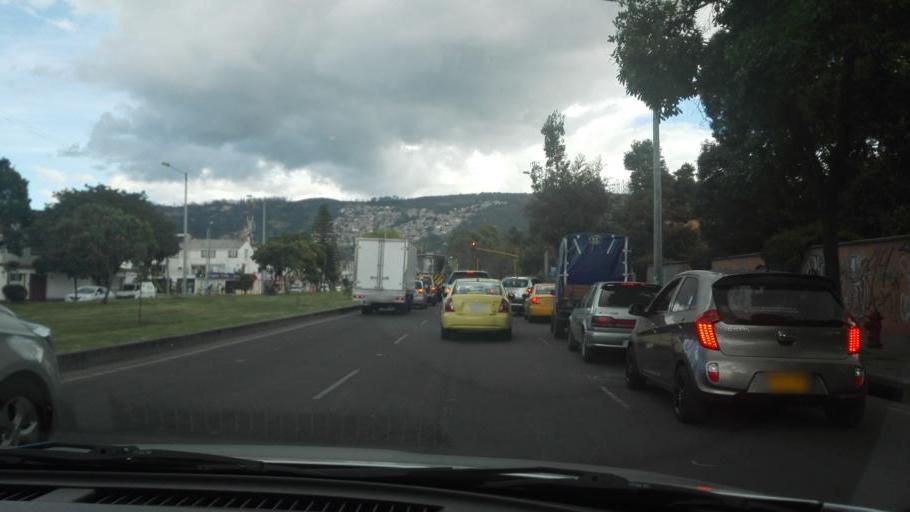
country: CO
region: Bogota D.C.
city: Barrio San Luis
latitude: 4.7367
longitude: -74.0447
